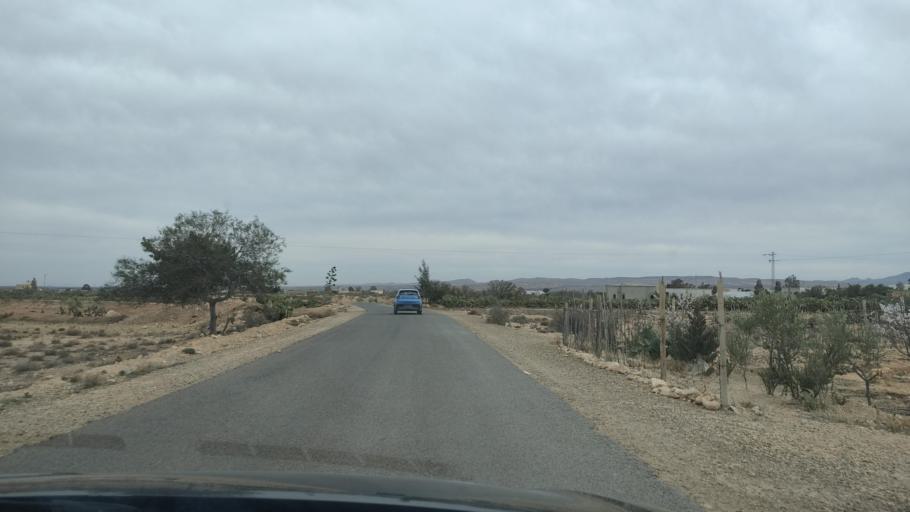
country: TN
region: Al Qasrayn
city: Kasserine
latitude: 35.2622
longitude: 8.9367
